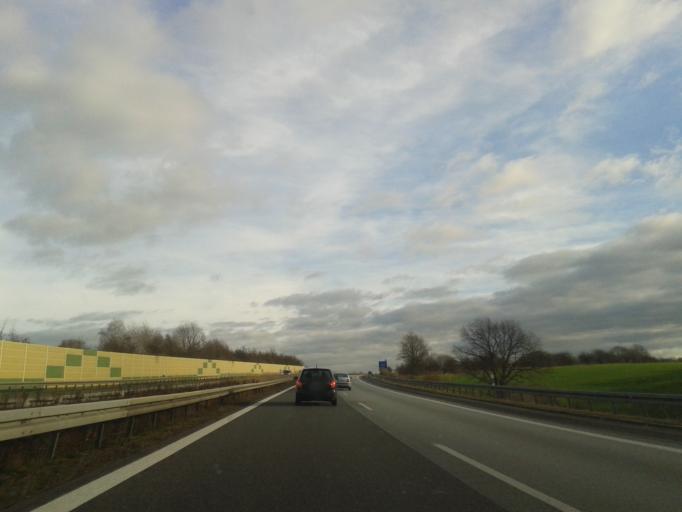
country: DE
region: Saxony
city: Goda
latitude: 51.2033
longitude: 14.3051
